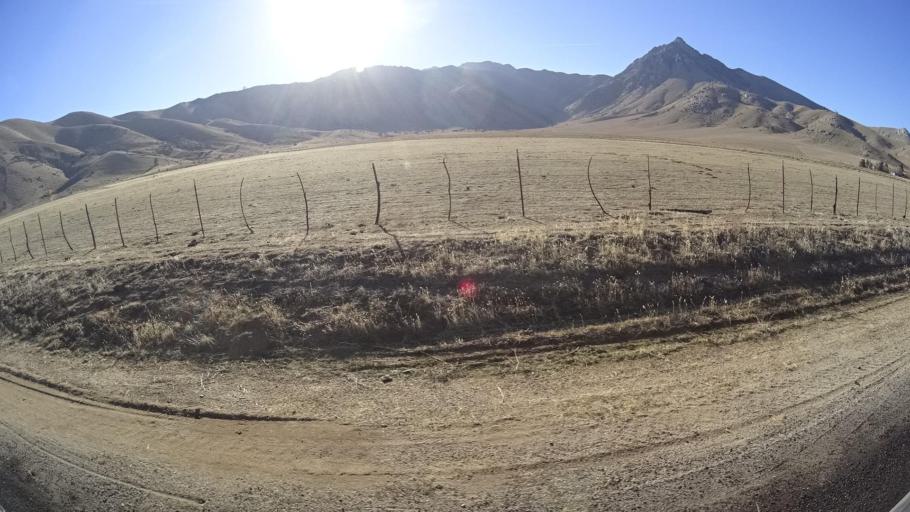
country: US
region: California
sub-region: Kern County
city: Weldon
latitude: 35.6216
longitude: -118.2564
